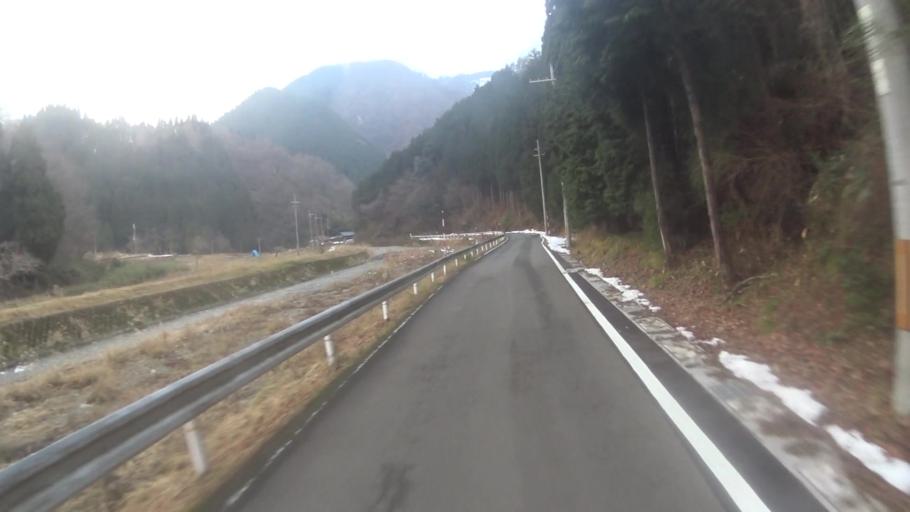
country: JP
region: Kyoto
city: Maizuru
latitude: 35.3900
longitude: 135.4714
